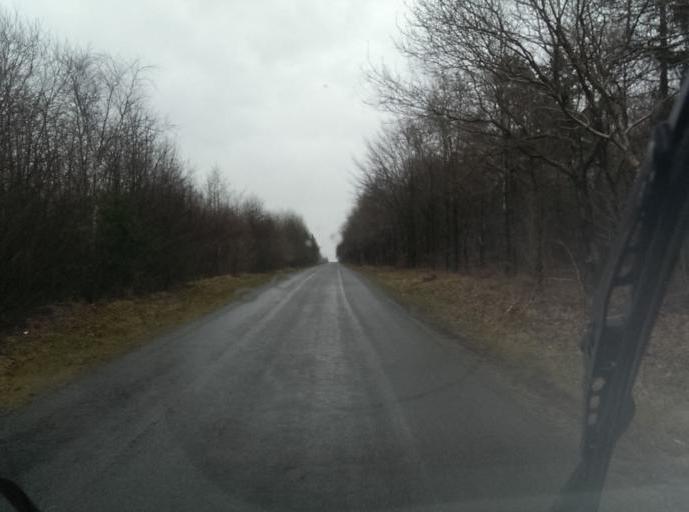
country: DK
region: Central Jutland
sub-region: Ringkobing-Skjern Kommune
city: Skjern
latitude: 56.0836
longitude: 8.4621
